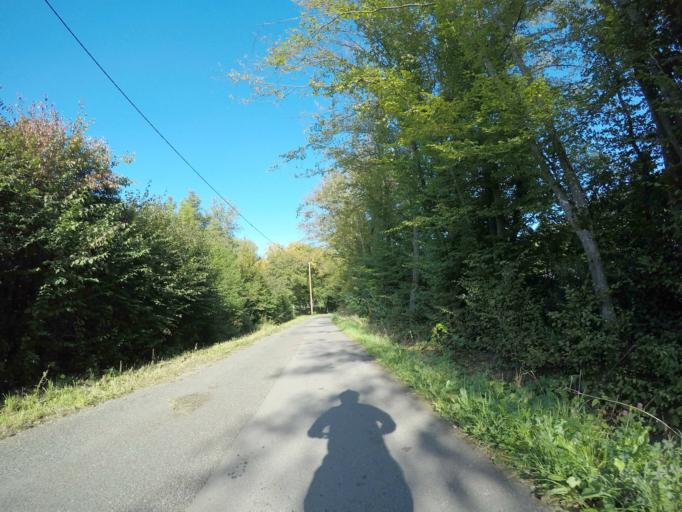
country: DE
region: Baden-Wuerttemberg
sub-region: Tuebingen Region
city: Reutlingen
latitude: 48.4722
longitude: 9.1895
